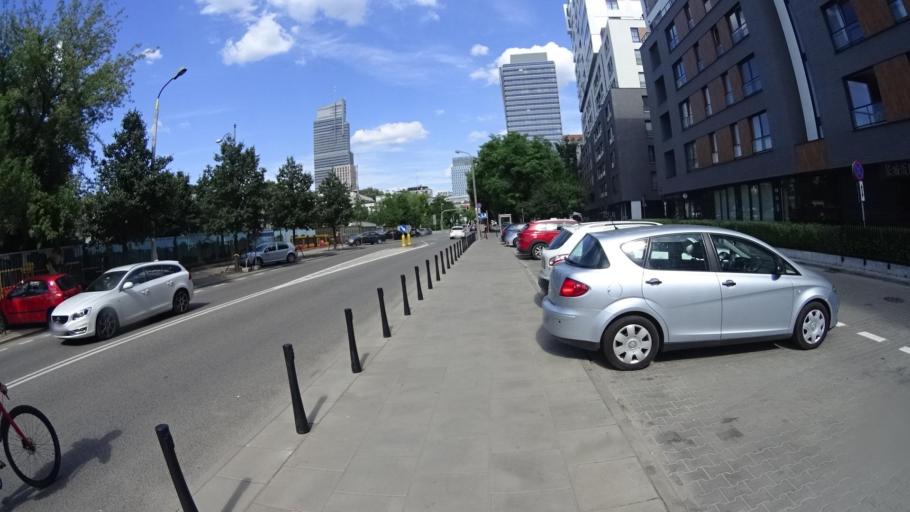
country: PL
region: Masovian Voivodeship
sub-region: Warszawa
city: Ochota
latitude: 52.2321
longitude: 20.9757
